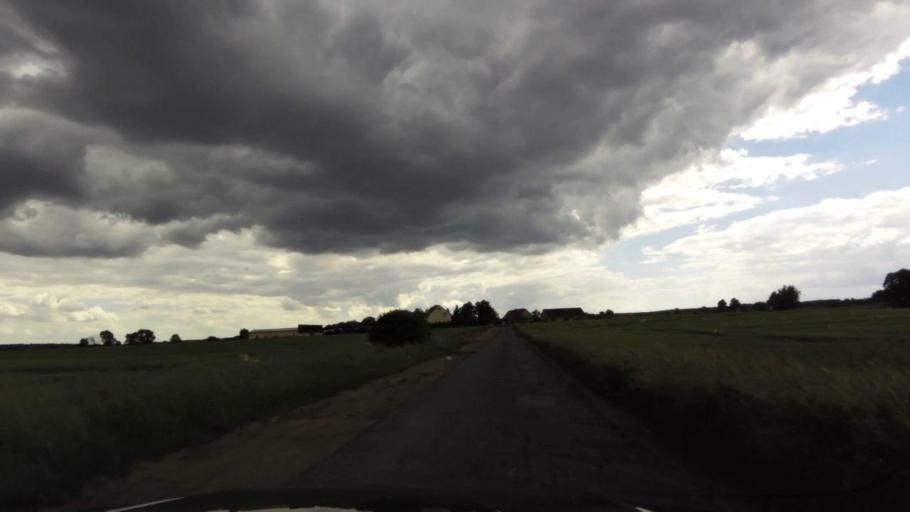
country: PL
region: West Pomeranian Voivodeship
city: Trzcinsko Zdroj
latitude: 52.9430
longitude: 14.6013
